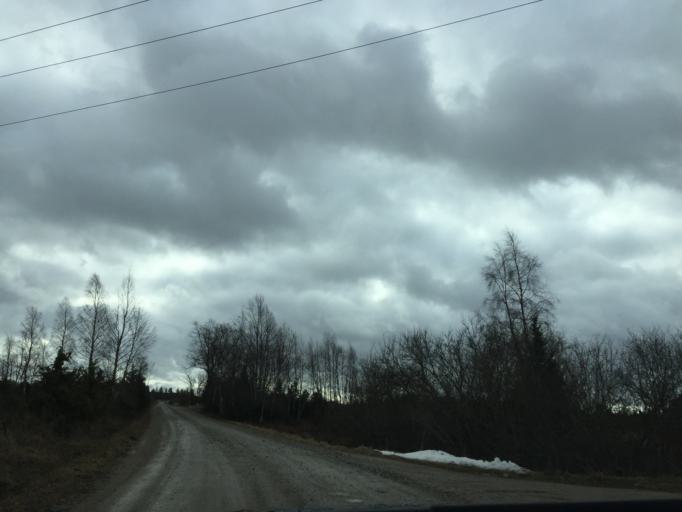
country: EE
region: Laeaene
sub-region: Haapsalu linn
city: Haapsalu
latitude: 58.6823
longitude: 23.5291
